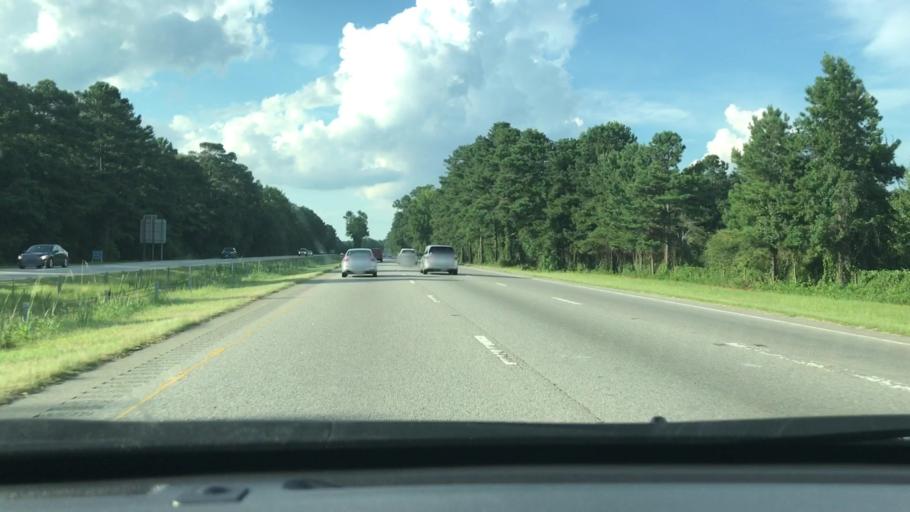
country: US
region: North Carolina
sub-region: Robeson County
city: Saint Pauls
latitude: 34.8145
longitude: -78.9851
